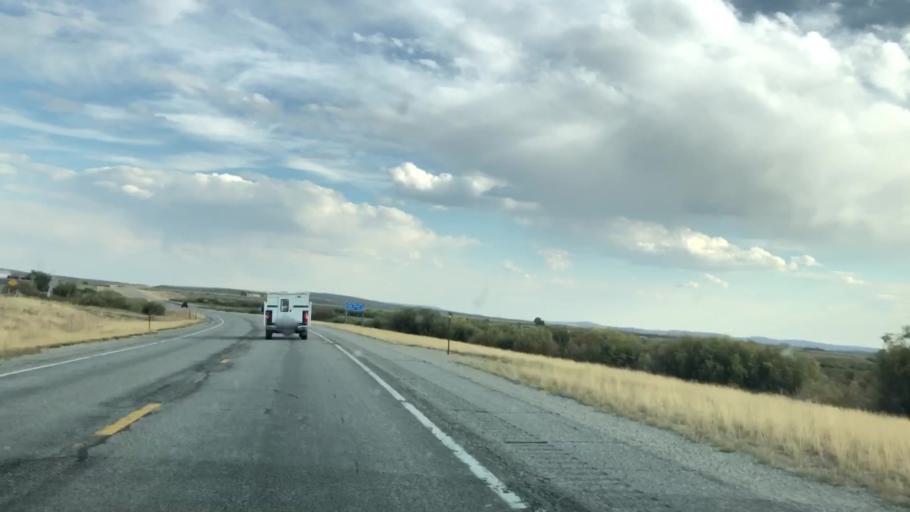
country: US
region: Wyoming
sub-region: Sublette County
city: Pinedale
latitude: 43.0218
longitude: -110.1223
